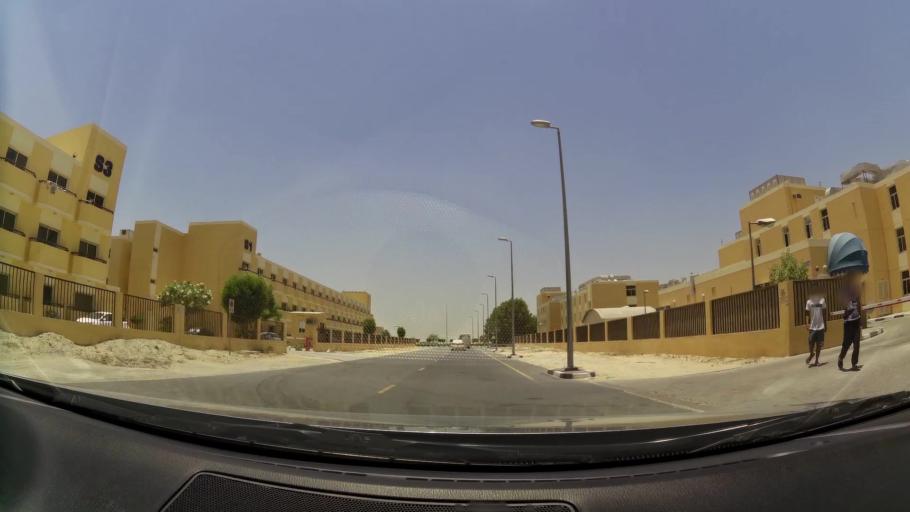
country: AE
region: Dubai
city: Dubai
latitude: 24.9869
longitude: 55.1830
